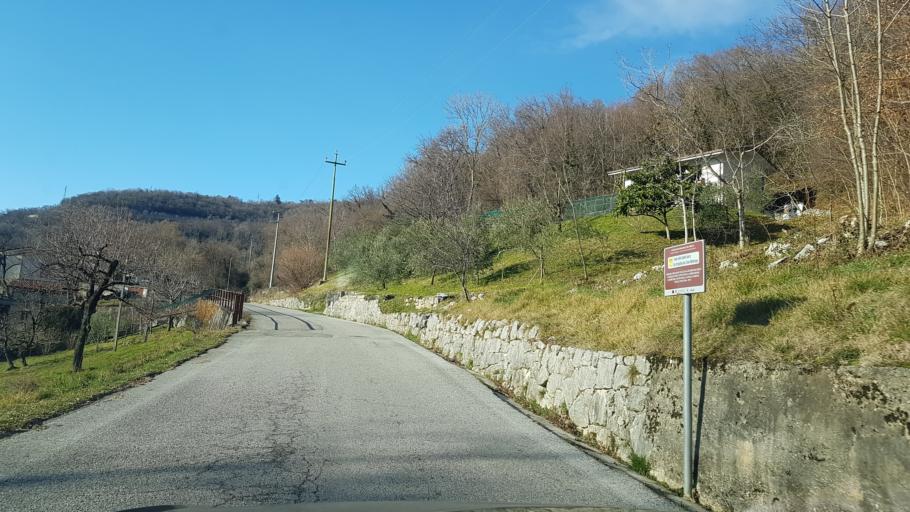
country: IT
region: Friuli Venezia Giulia
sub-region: Provincia di Udine
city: Forgaria nel Friuli
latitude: 46.2270
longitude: 13.0035
